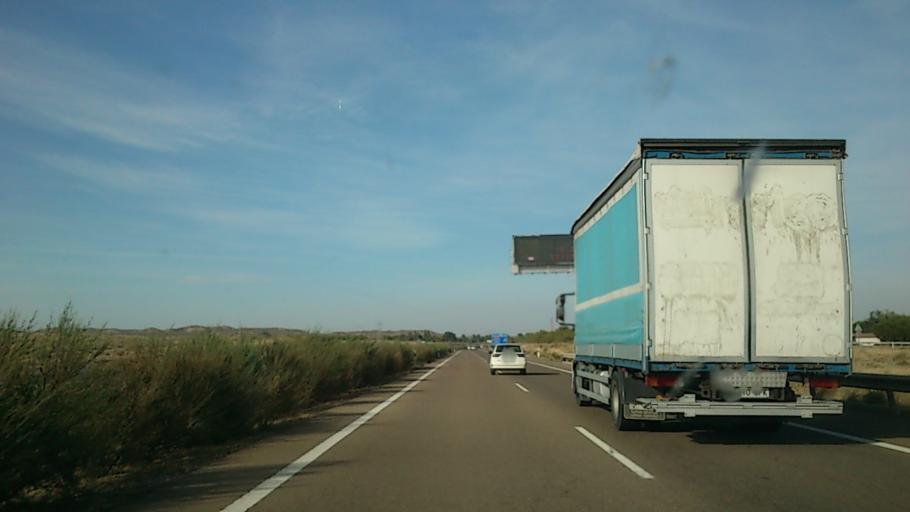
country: ES
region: Aragon
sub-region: Provincia de Zaragoza
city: Cadrete
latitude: 41.5805
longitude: -0.9577
